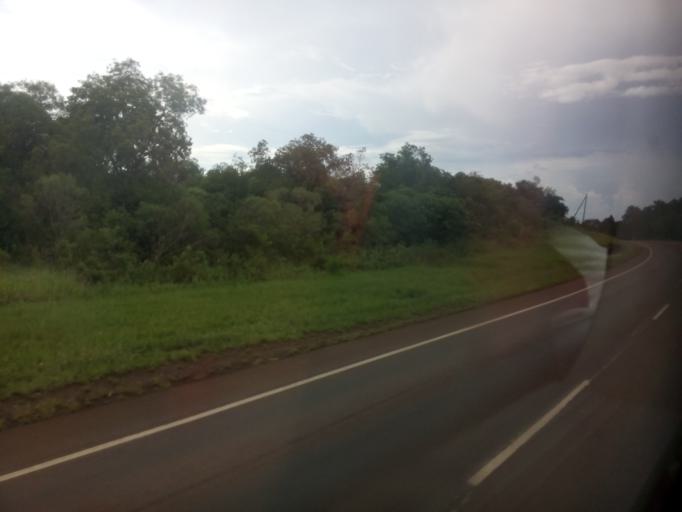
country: AR
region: Misiones
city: Santa Ana
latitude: -27.4040
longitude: -55.6026
